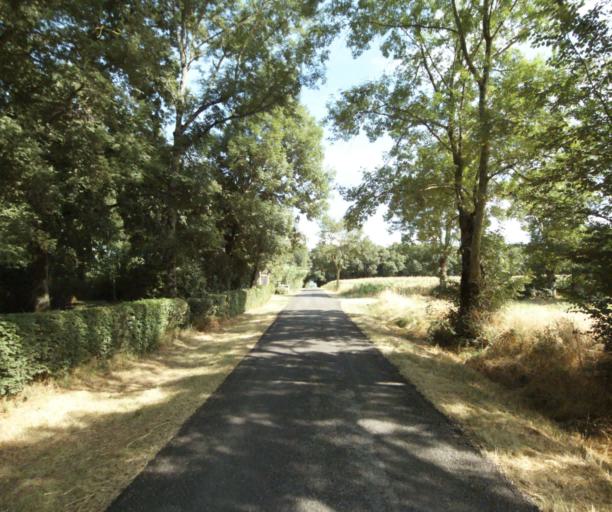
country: FR
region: Midi-Pyrenees
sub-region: Departement du Tarn
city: Soreze
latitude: 43.5107
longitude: 2.0543
